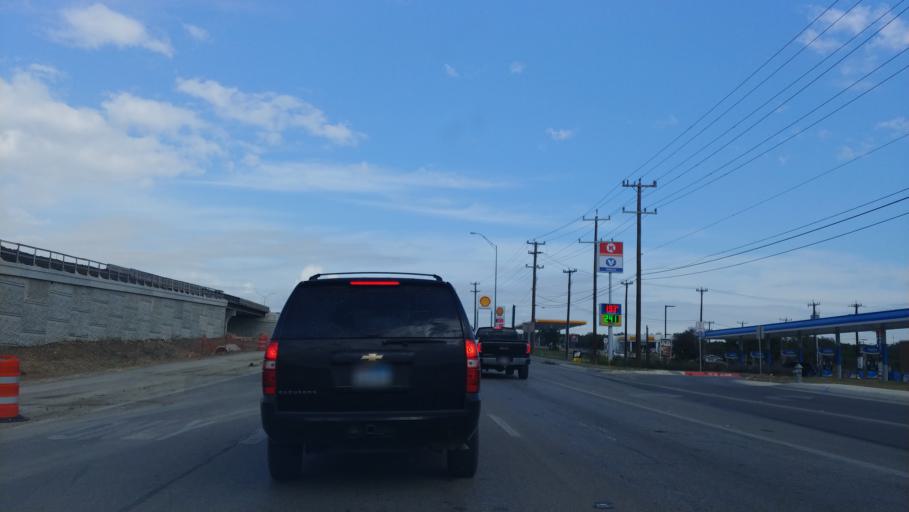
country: US
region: Texas
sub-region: Bexar County
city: Leon Valley
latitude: 29.4467
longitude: -98.7108
